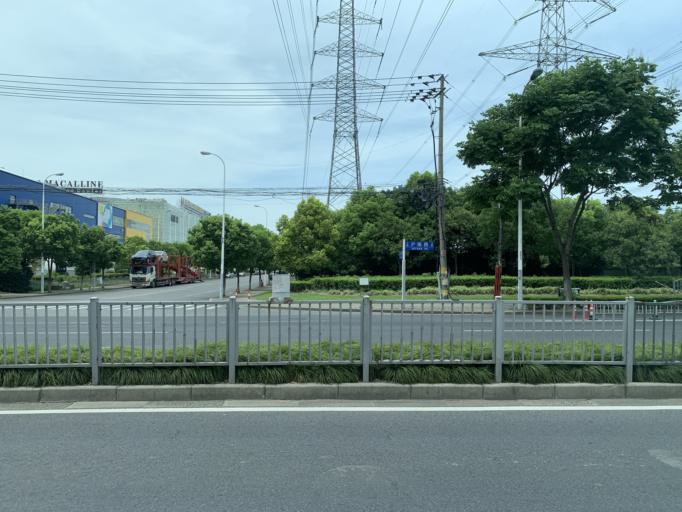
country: CN
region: Shanghai Shi
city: Kangqiao
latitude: 31.1633
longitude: 121.5594
